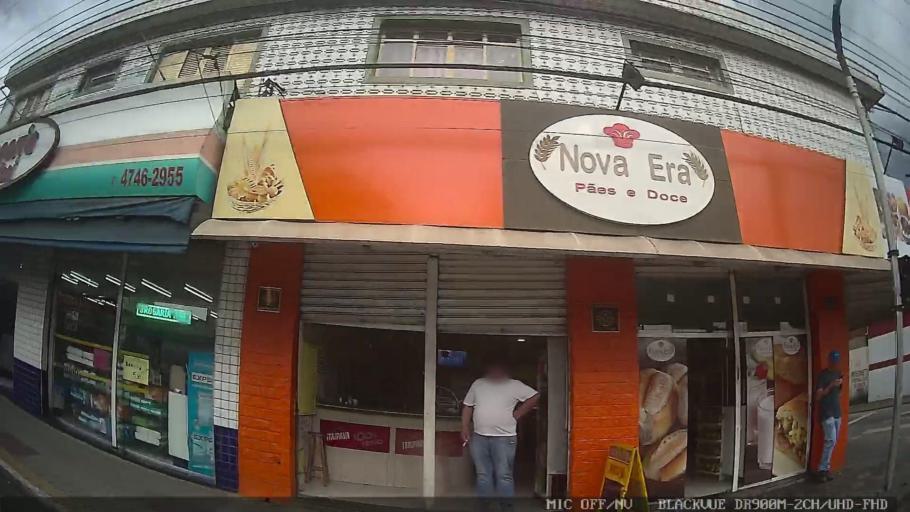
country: BR
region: Sao Paulo
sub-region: Suzano
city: Suzano
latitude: -23.5498
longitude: -46.3072
